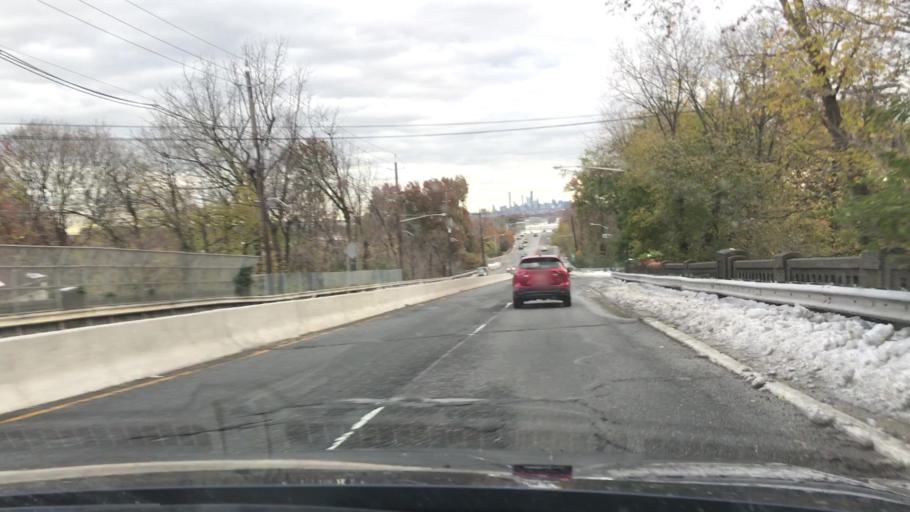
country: US
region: New Jersey
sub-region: Bergen County
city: Hasbrouck Heights
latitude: 40.8689
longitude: -74.0653
